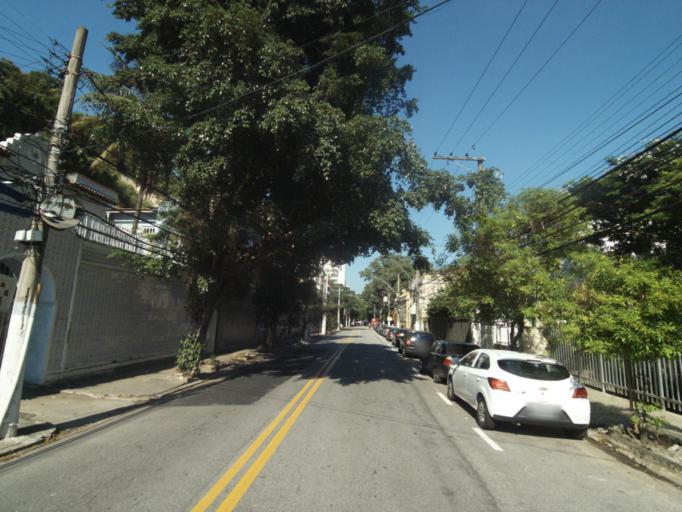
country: BR
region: Rio de Janeiro
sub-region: Niteroi
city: Niteroi
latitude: -22.9039
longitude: -43.1287
